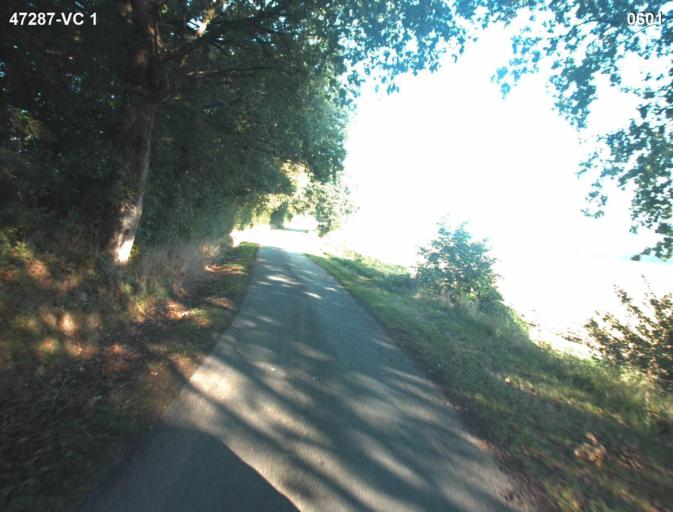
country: FR
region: Aquitaine
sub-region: Departement du Lot-et-Garonne
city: Laplume
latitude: 44.1286
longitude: 0.4558
